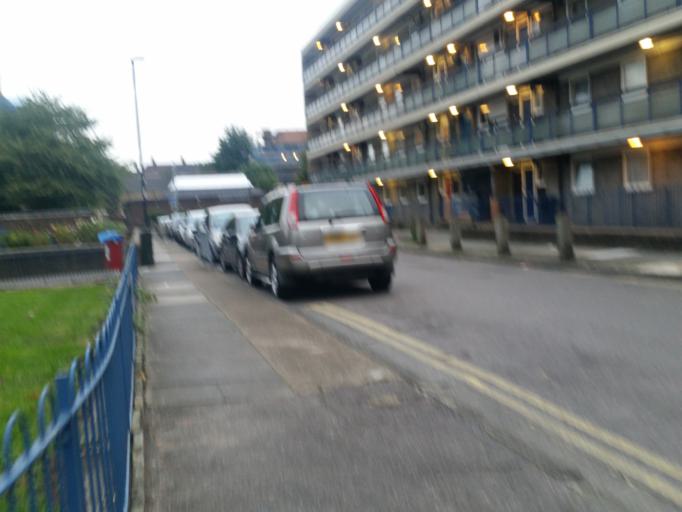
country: GB
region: England
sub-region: Greater London
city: Poplar
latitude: 51.4827
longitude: -0.0279
